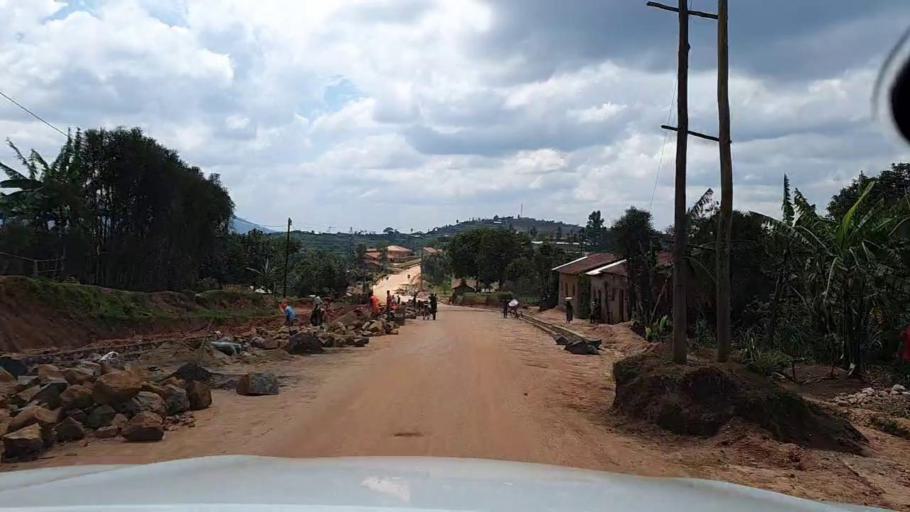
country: RW
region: Southern Province
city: Butare
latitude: -2.6893
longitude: 29.5662
